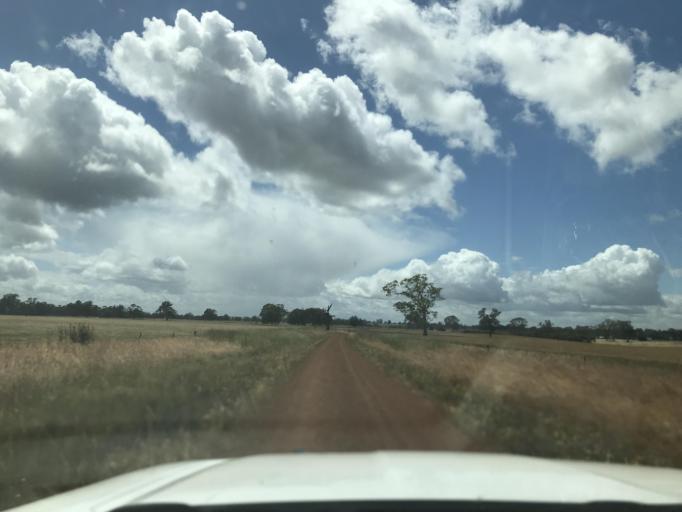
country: AU
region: South Australia
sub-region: Wattle Range
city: Penola
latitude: -37.1835
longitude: 141.4636
